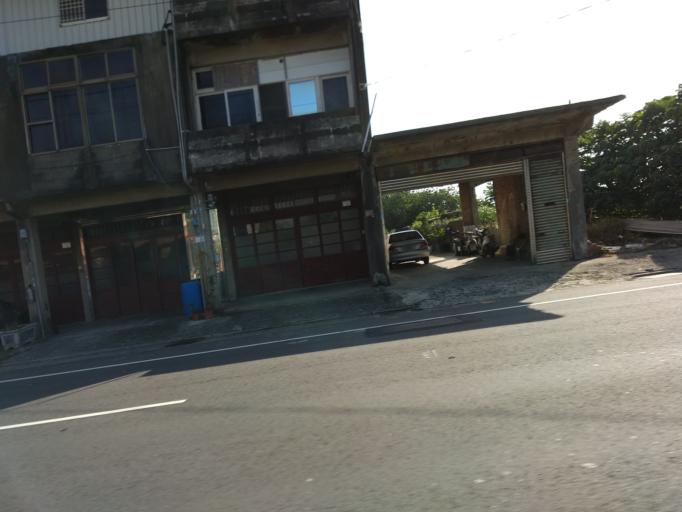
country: TW
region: Taiwan
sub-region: Hsinchu
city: Zhubei
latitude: 24.9866
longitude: 121.0484
